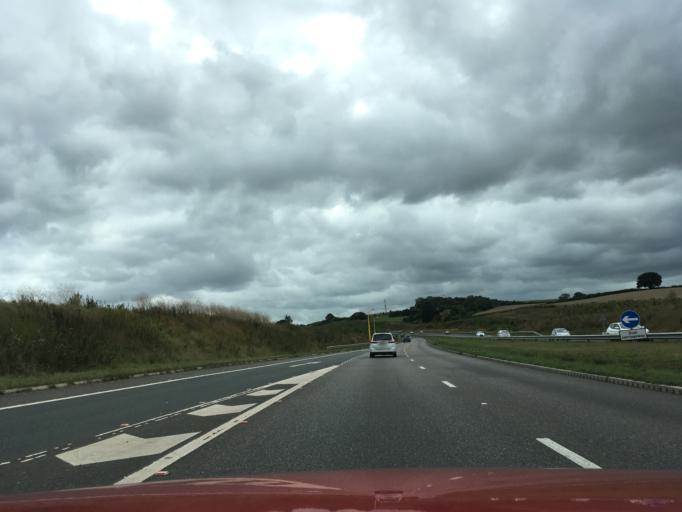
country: GB
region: England
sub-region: Devon
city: Kingskerswell
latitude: 50.5104
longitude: -3.5879
